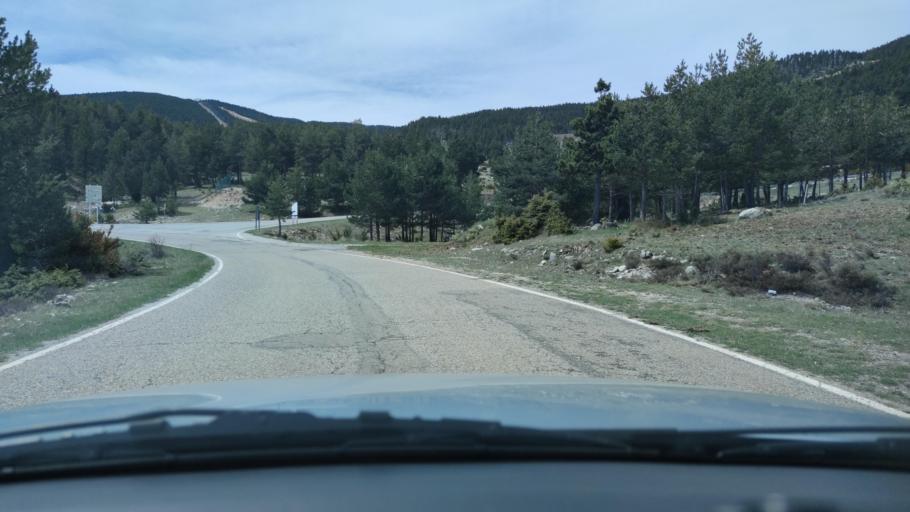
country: ES
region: Catalonia
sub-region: Provincia de Lleida
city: Gosol
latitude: 42.1802
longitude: 1.5570
